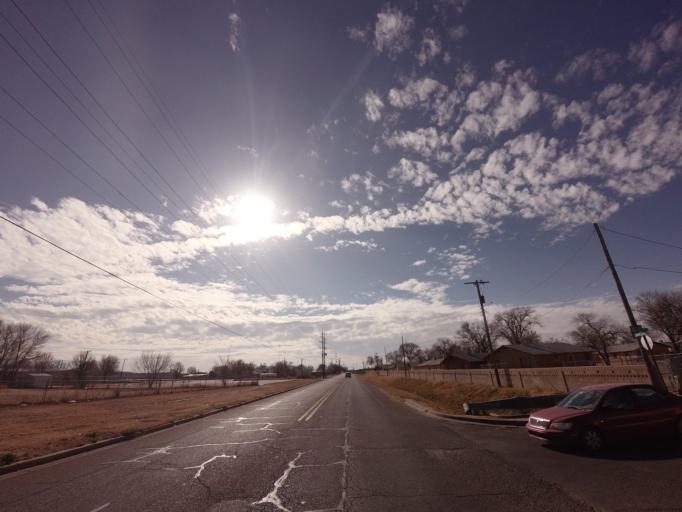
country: US
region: New Mexico
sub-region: Curry County
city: Clovis
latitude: 34.4079
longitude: -103.2318
